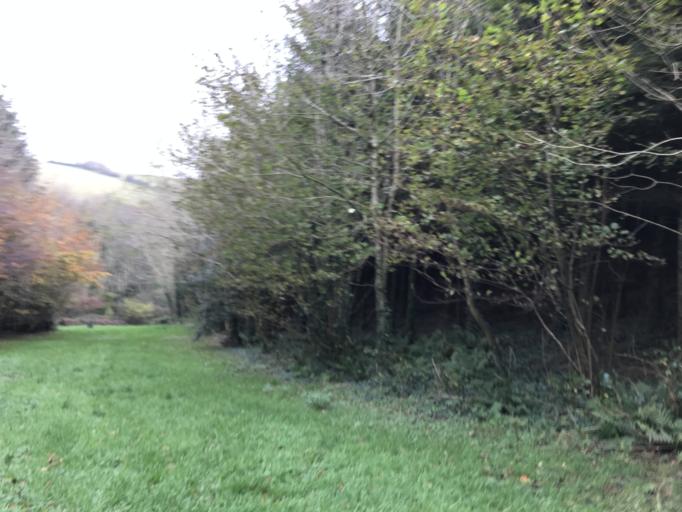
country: GB
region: England
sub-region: Devon
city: Braunton
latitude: 51.1179
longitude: -4.1165
